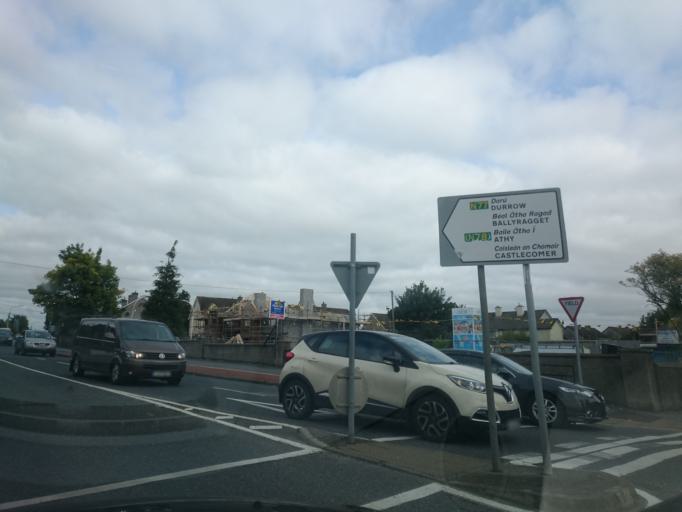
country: IE
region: Leinster
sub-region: Kilkenny
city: Kilkenny
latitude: 52.6597
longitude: -7.2491
